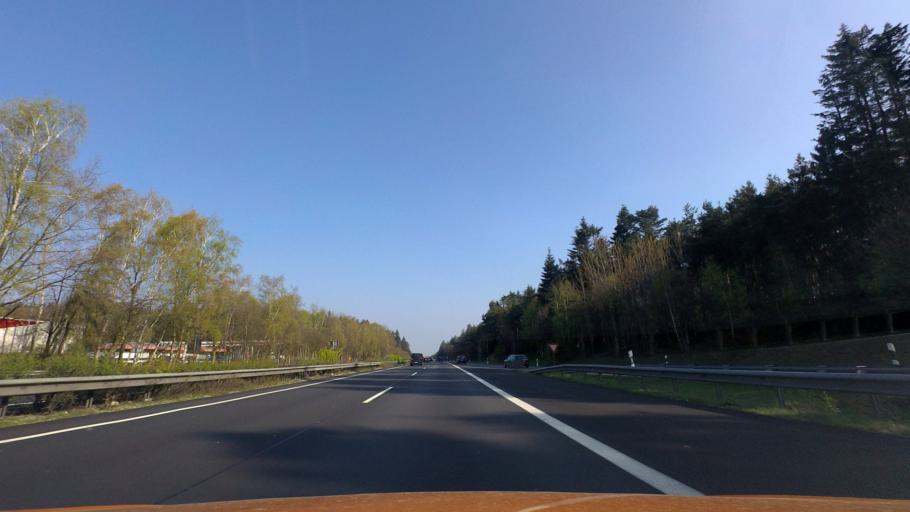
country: DE
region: Lower Saxony
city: Holdorf
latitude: 52.5420
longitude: 8.1139
